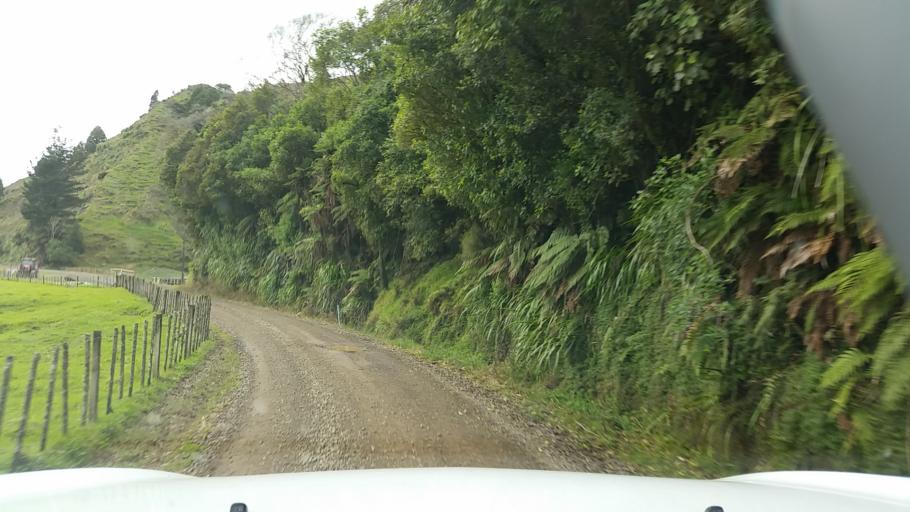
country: NZ
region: Taranaki
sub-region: New Plymouth District
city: Waitara
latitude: -38.8632
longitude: 174.6607
